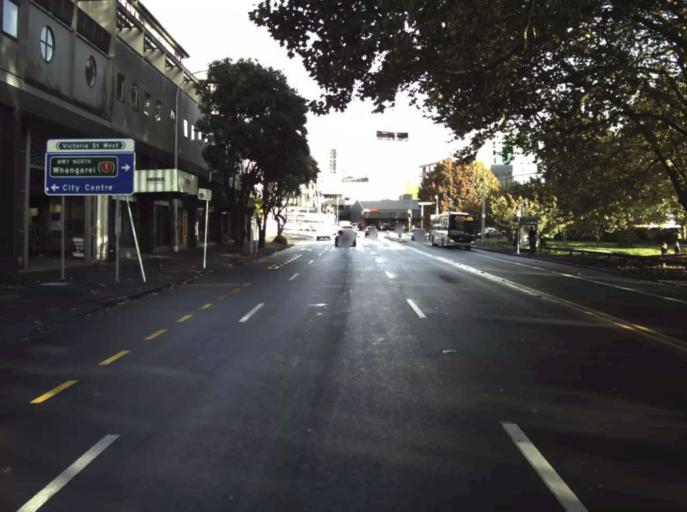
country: NZ
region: Auckland
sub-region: Auckland
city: Auckland
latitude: -36.8470
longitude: 174.7565
